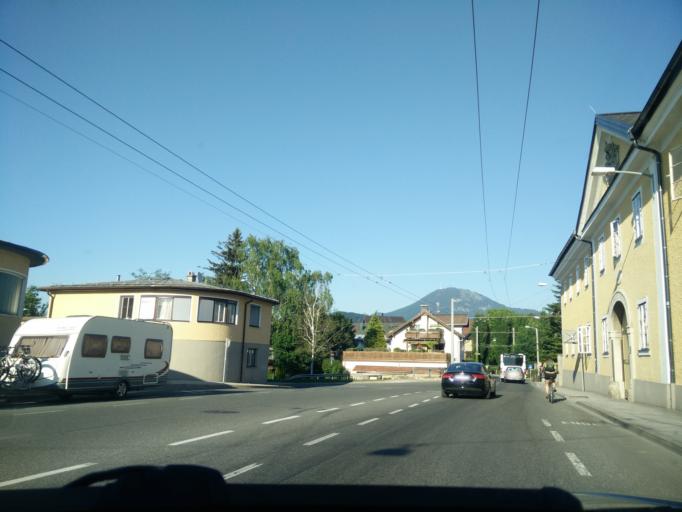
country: AT
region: Salzburg
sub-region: Salzburg Stadt
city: Salzburg
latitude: 47.7959
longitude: 13.0182
